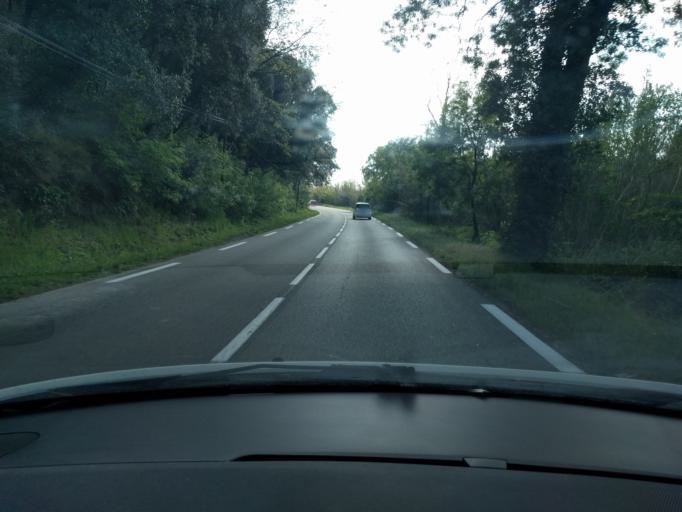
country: FR
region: Provence-Alpes-Cote d'Azur
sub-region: Departement du Var
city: Pierrefeu-du-Var
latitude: 43.2081
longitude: 6.1382
